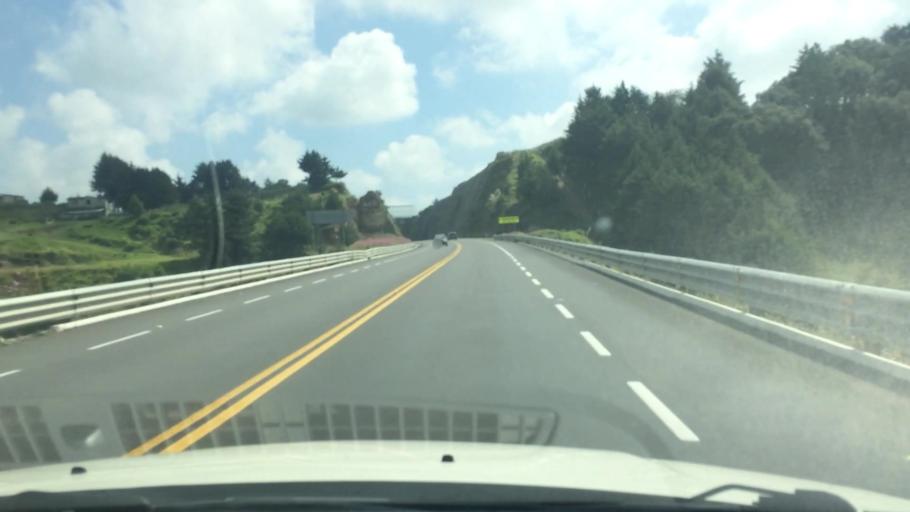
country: MX
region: Mexico
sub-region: Villa Victoria
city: Colonia Doctor Gustavo Baz
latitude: 19.3626
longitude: -99.9487
